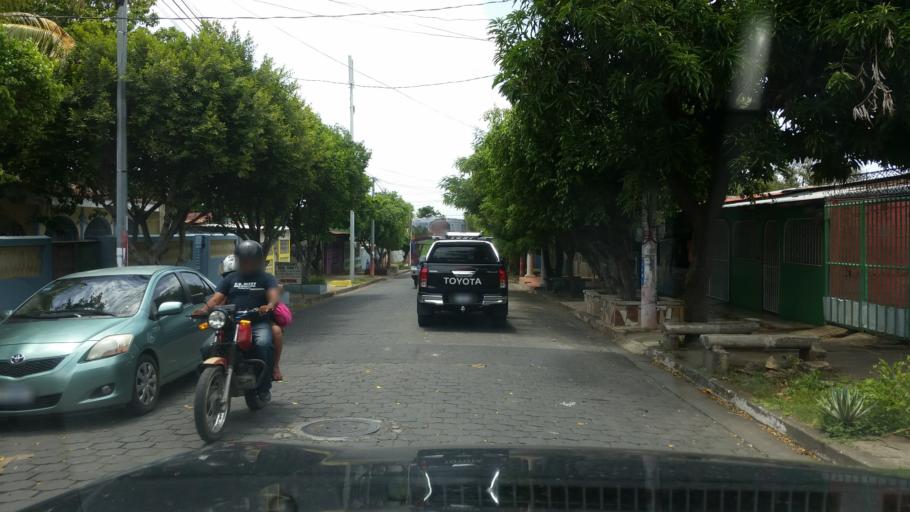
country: NI
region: Managua
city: Managua
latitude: 12.1440
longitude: -86.2096
